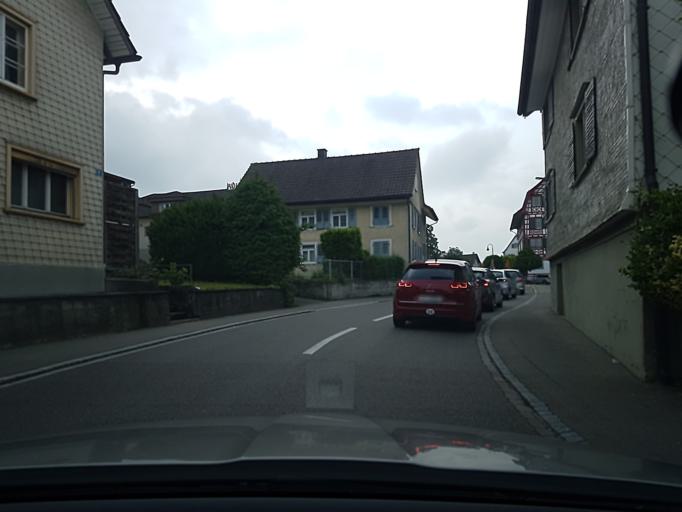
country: CH
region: Thurgau
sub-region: Arbon District
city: Roggwil
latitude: 47.4998
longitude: 9.3967
